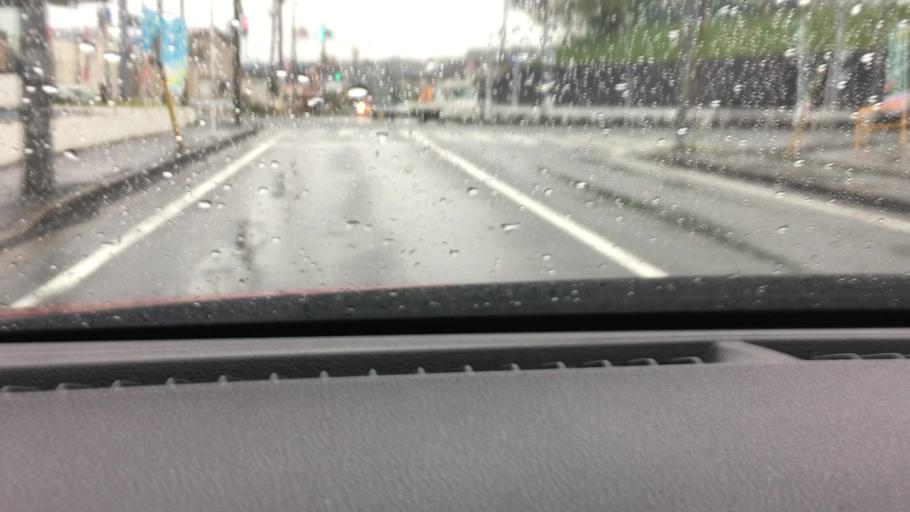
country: JP
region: Chiba
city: Kisarazu
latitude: 35.3744
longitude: 139.9374
